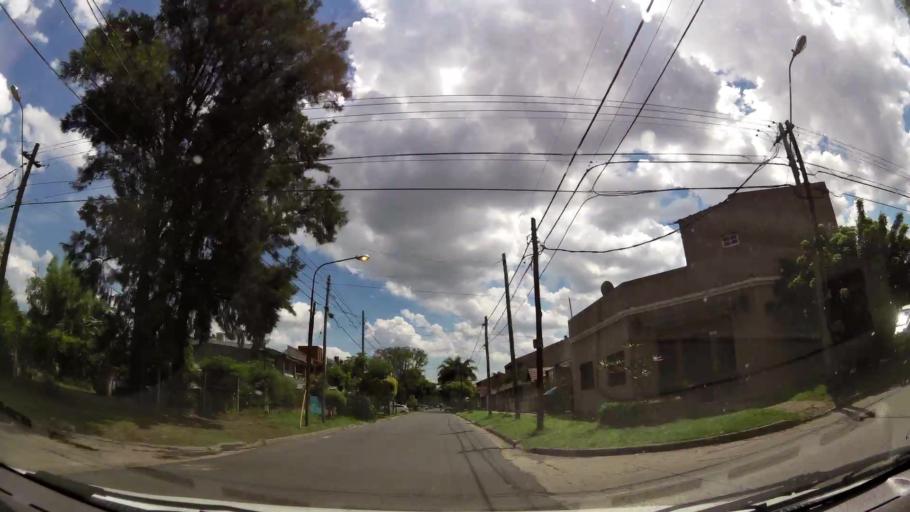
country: AR
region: Buenos Aires
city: Ituzaingo
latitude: -34.6477
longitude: -58.6717
